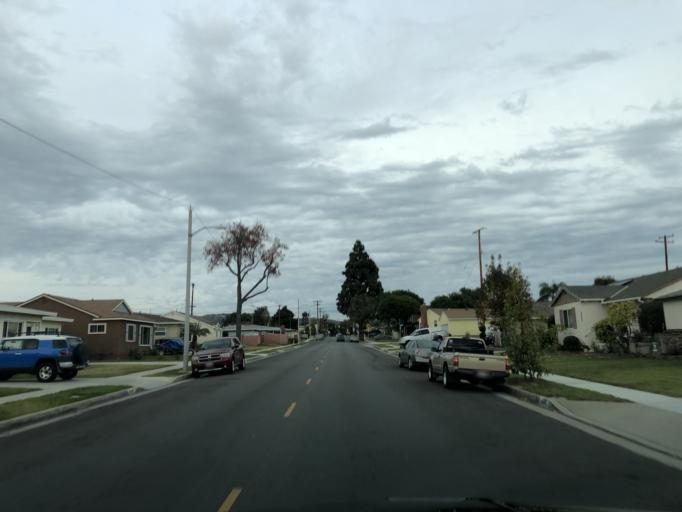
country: US
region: California
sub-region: Los Angeles County
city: South Whittier
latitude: 33.9500
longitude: -118.0324
